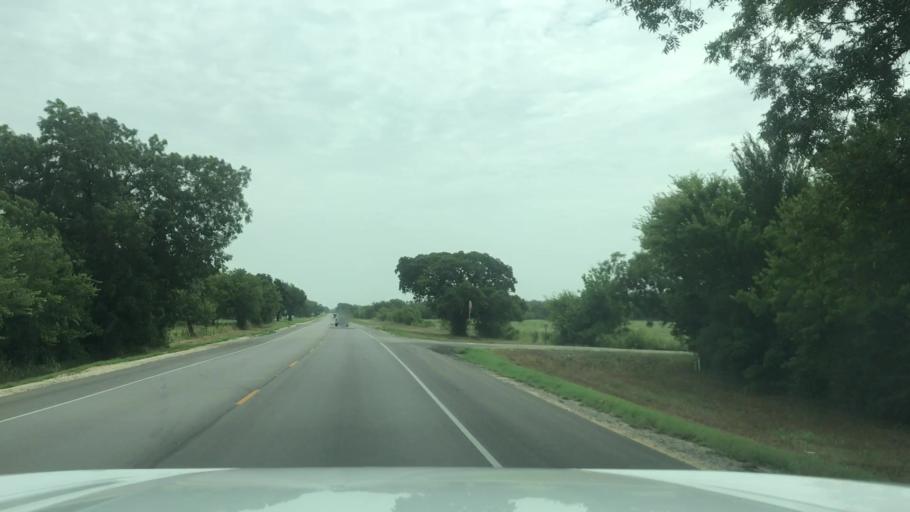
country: US
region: Texas
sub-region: Erath County
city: Dublin
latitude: 32.0887
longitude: -98.2953
